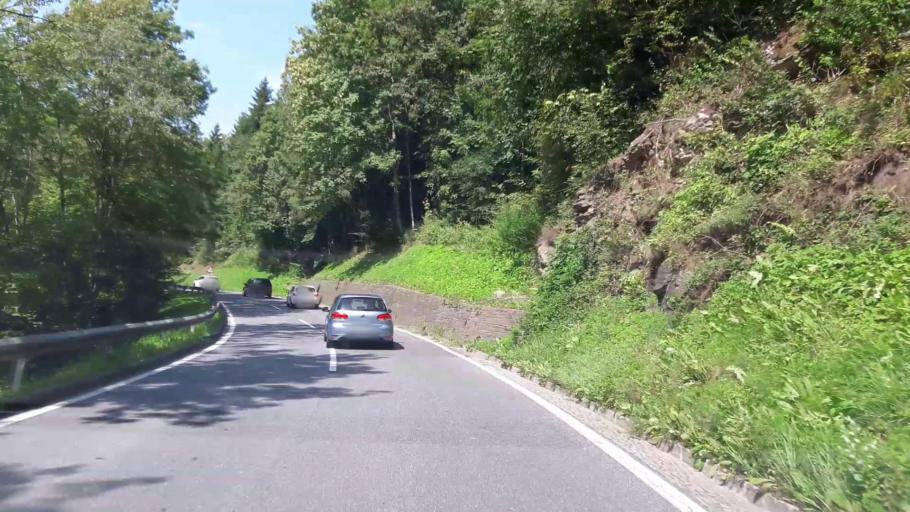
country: AT
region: Styria
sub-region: Politischer Bezirk Weiz
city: Koglhof
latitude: 47.3122
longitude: 15.6947
